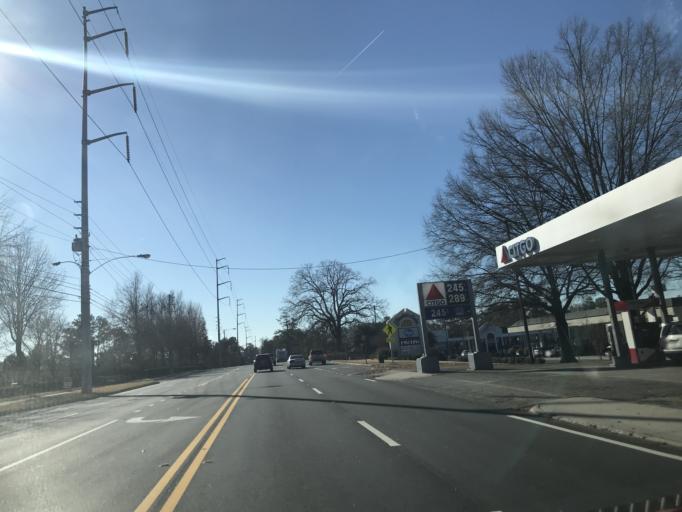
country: US
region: Georgia
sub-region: Fulton County
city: Sandy Springs
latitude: 33.8919
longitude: -84.3811
